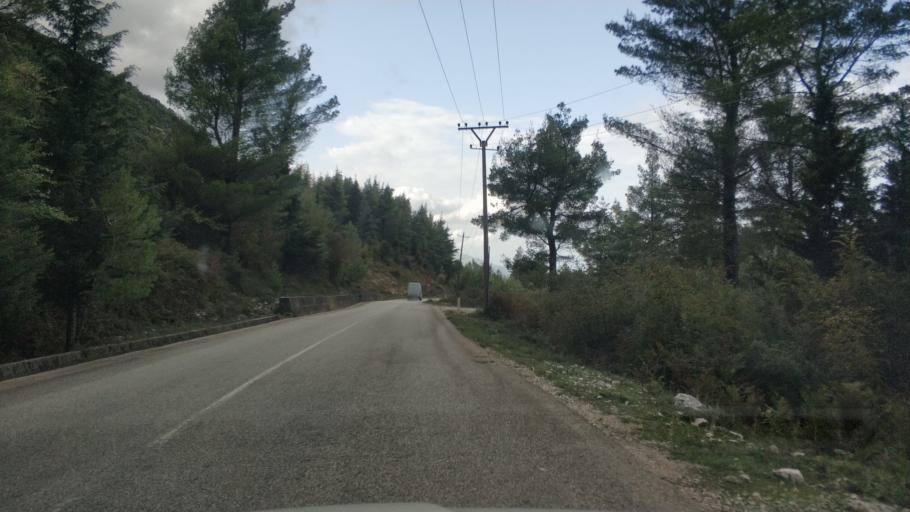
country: AL
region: Vlore
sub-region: Rrethi i Vlores
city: Orikum
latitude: 40.2571
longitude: 19.5285
